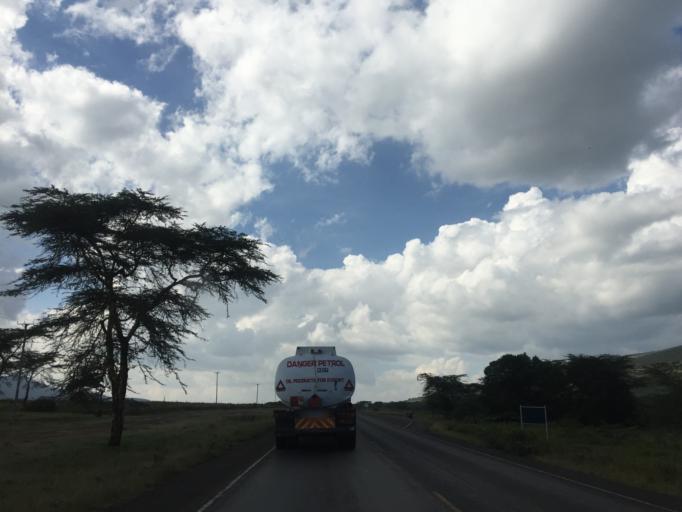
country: KE
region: Nakuru
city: Kijabe
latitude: -0.9451
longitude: 36.5456
